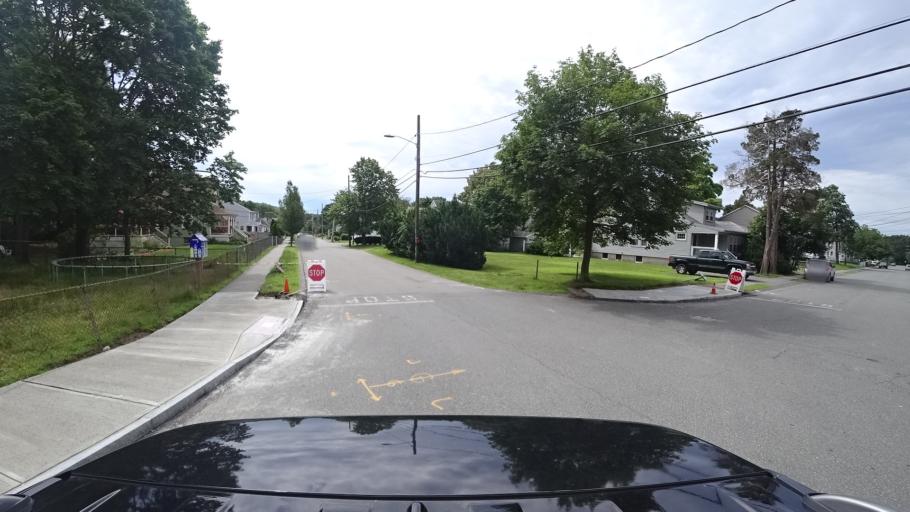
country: US
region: Massachusetts
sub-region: Norfolk County
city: Dedham
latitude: 42.2300
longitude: -71.1427
